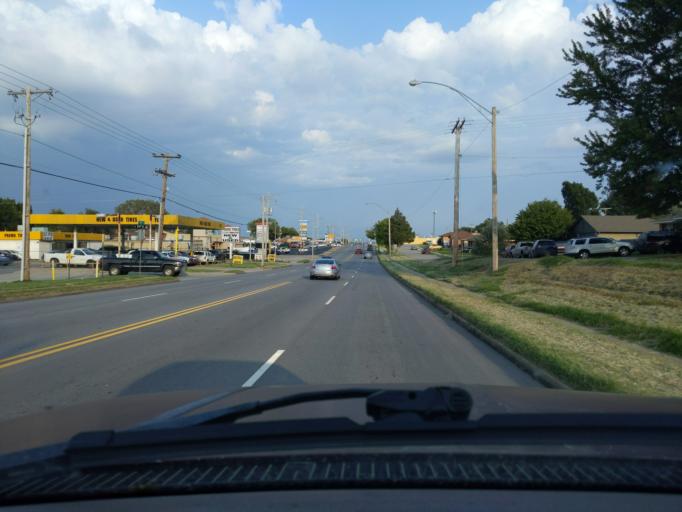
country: US
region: Oklahoma
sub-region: Tulsa County
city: Tulsa
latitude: 36.1334
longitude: -95.8916
